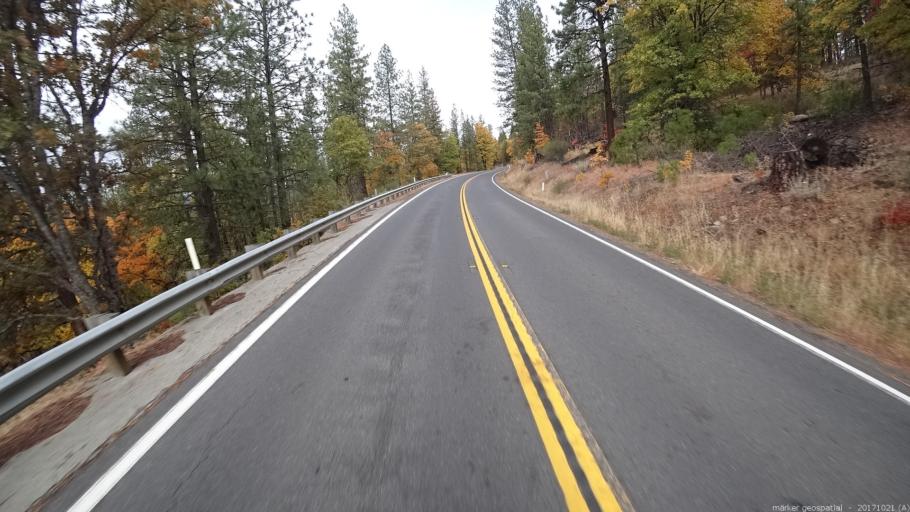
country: US
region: California
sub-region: Shasta County
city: Burney
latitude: 41.0260
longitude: -121.6253
